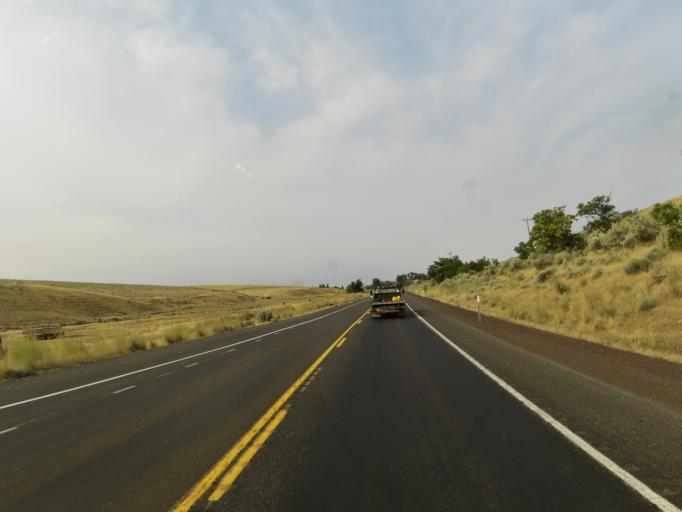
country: US
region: Oregon
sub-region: Sherman County
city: Moro
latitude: 45.4944
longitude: -120.7093
